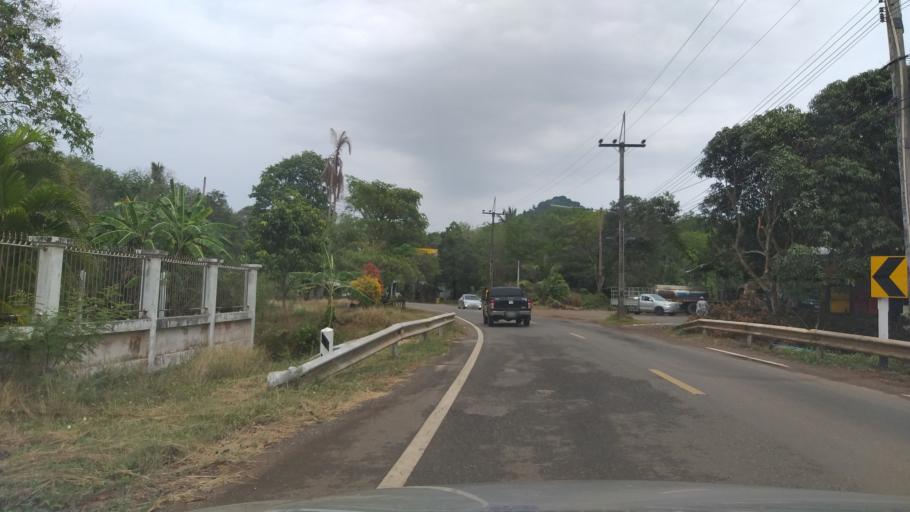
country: TH
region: Trat
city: Laem Ngop
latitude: 12.2149
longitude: 102.3041
